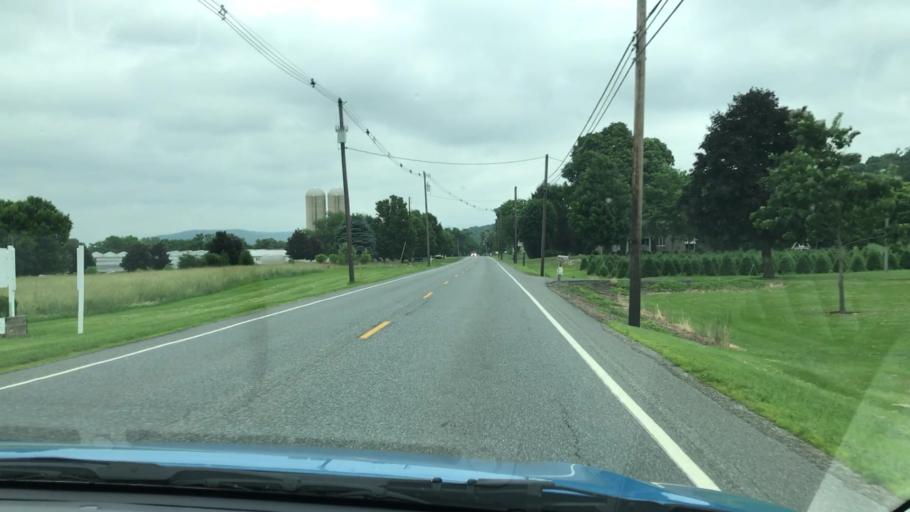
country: US
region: New Jersey
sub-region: Warren County
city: Belvidere
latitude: 40.8109
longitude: -75.0660
